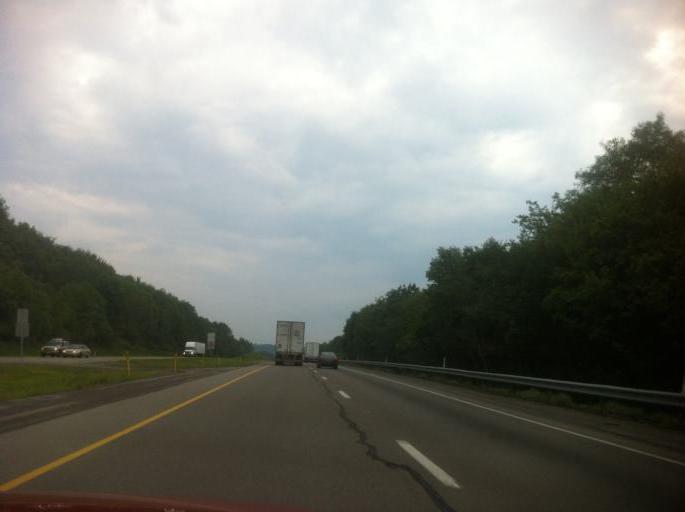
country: US
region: Pennsylvania
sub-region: Jefferson County
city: Brookville
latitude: 41.1849
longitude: -79.1632
